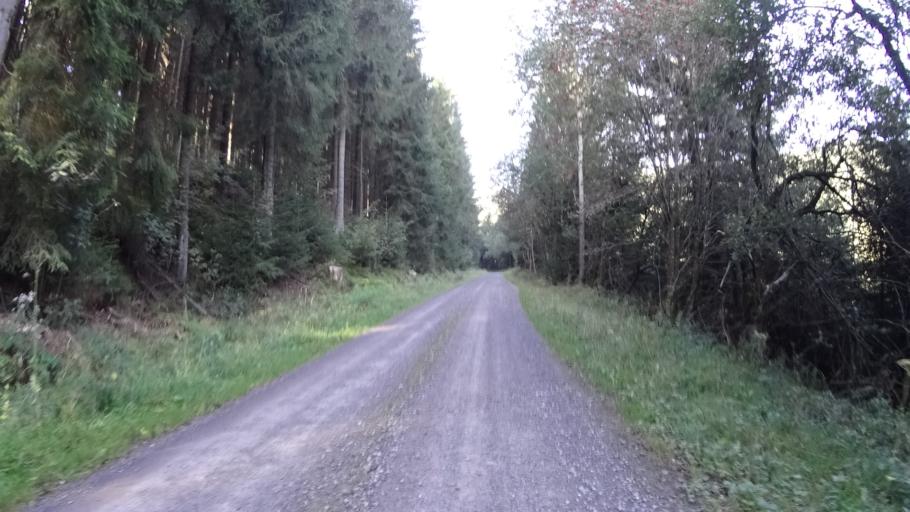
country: DE
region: Thuringia
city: Neuhaus
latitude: 50.6437
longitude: 10.9418
